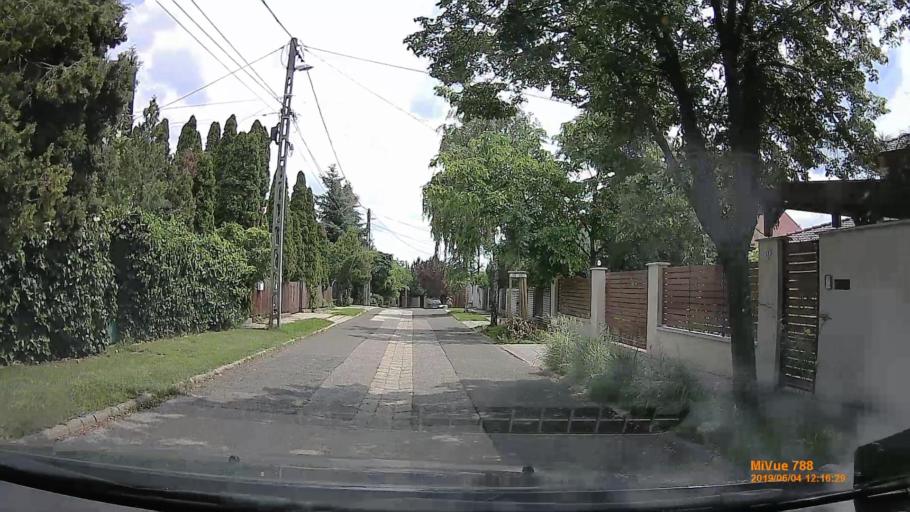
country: HU
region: Budapest
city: Budapest XXII. keruelet
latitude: 47.4278
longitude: 19.0183
